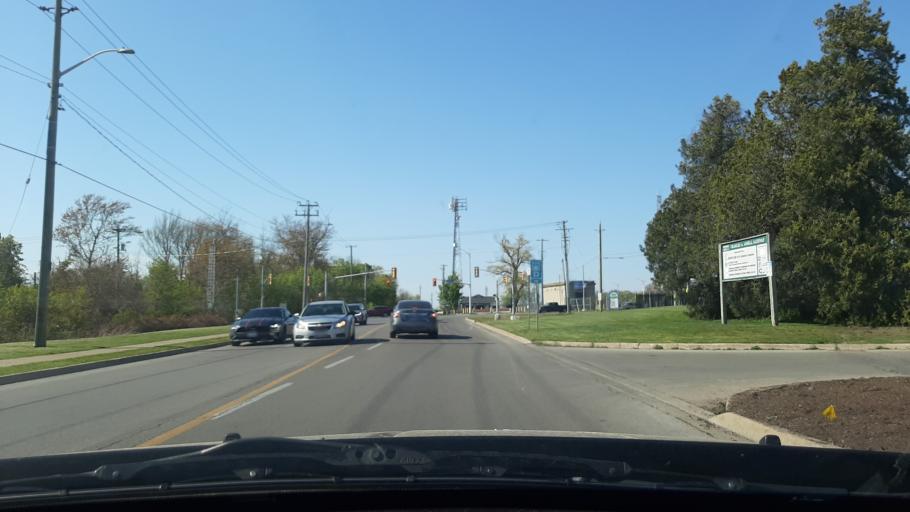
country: CA
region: Ontario
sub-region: Regional Municipality of Niagara
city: St. Catharines
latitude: 43.2148
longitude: -79.2136
